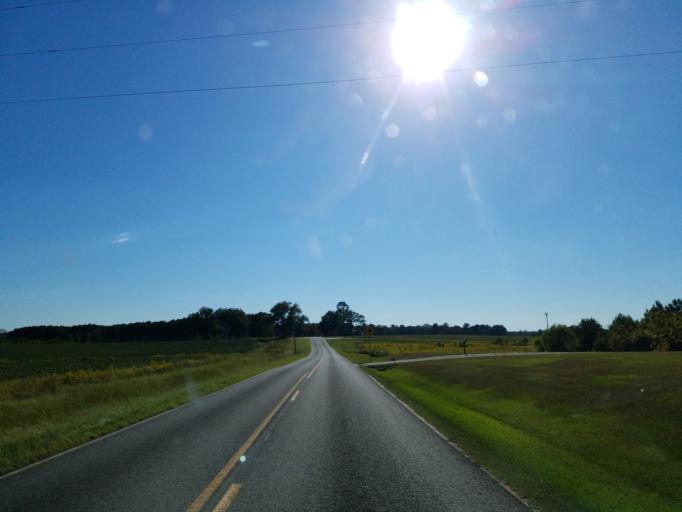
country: US
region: Georgia
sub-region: Dooly County
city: Unadilla
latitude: 32.2482
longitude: -83.7955
